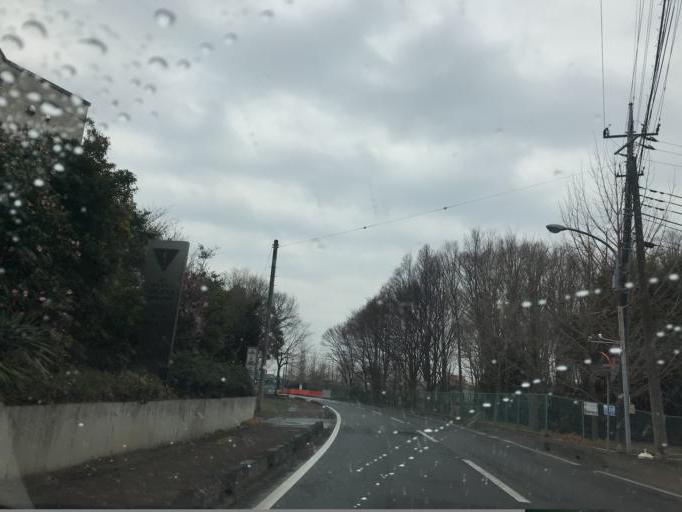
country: JP
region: Ibaraki
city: Moriya
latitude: 35.9503
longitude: 139.9778
